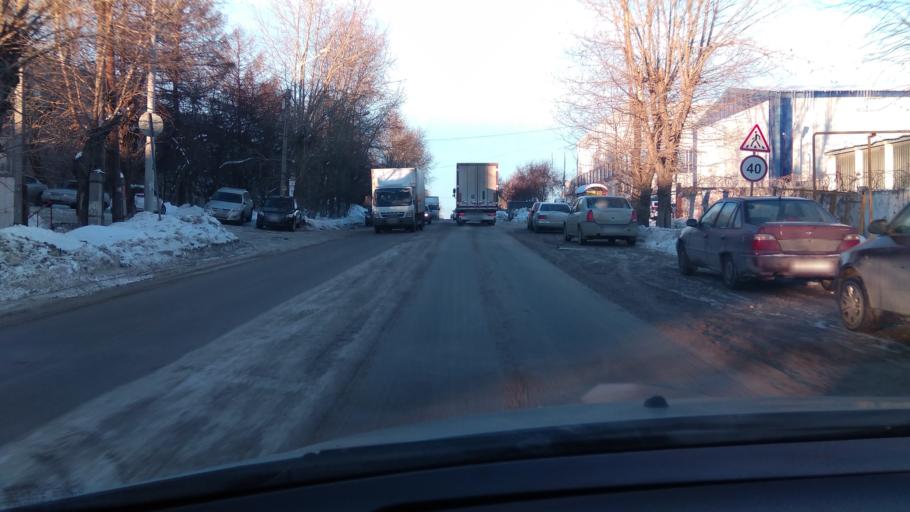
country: RU
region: Sverdlovsk
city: Sovkhoznyy
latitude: 56.7594
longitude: 60.6270
